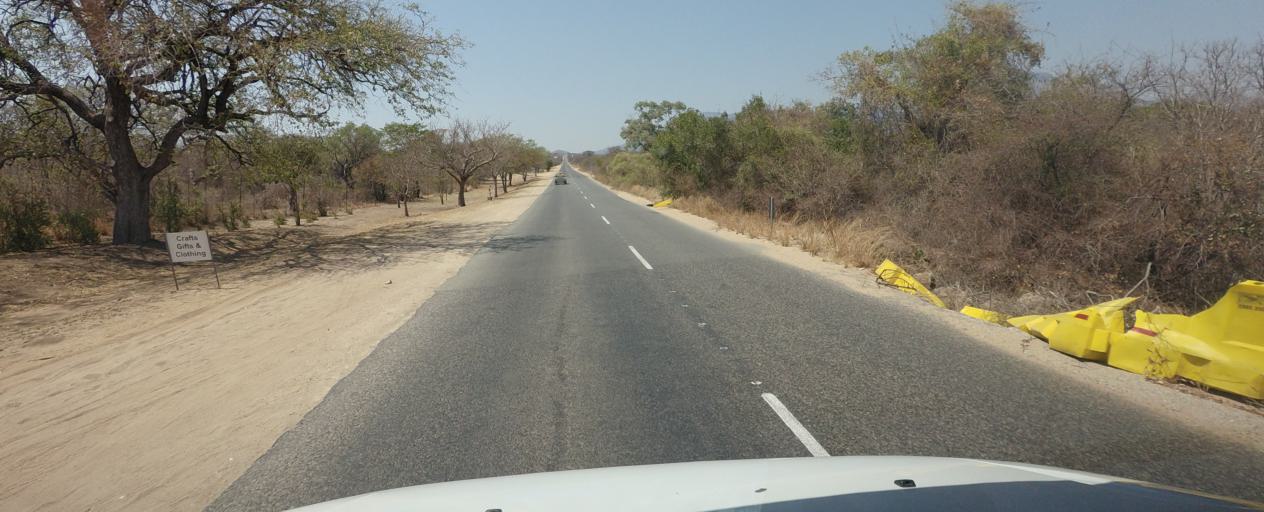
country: ZA
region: Limpopo
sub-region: Mopani District Municipality
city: Hoedspruit
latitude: -24.4670
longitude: 30.8747
